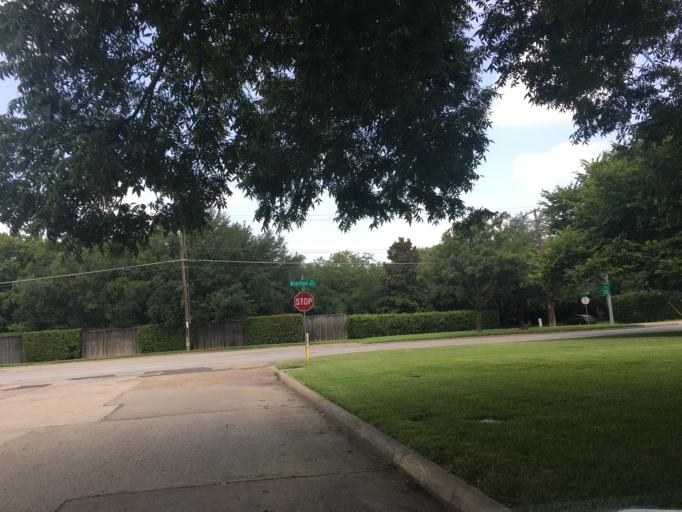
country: US
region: Texas
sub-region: Dallas County
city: University Park
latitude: 32.8722
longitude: -96.8036
